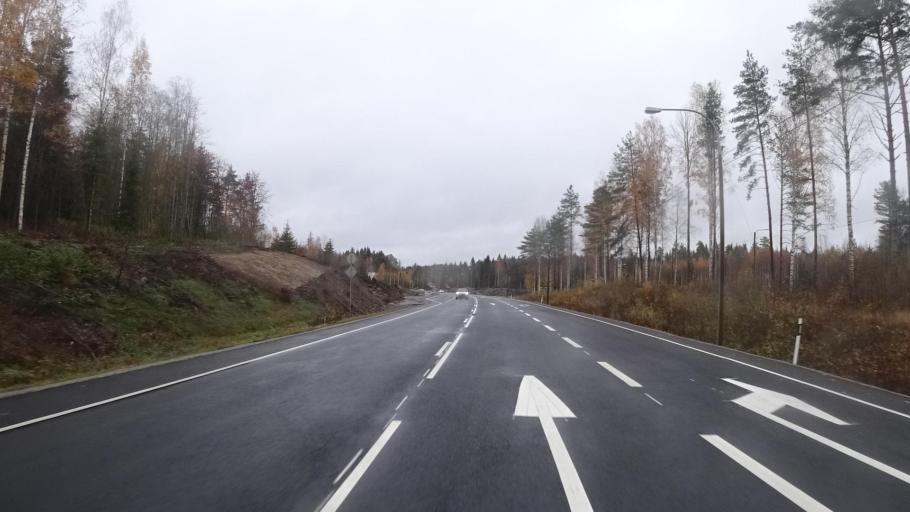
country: FI
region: Northern Savo
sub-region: Varkaus
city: Varkaus
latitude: 62.3143
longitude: 27.9976
